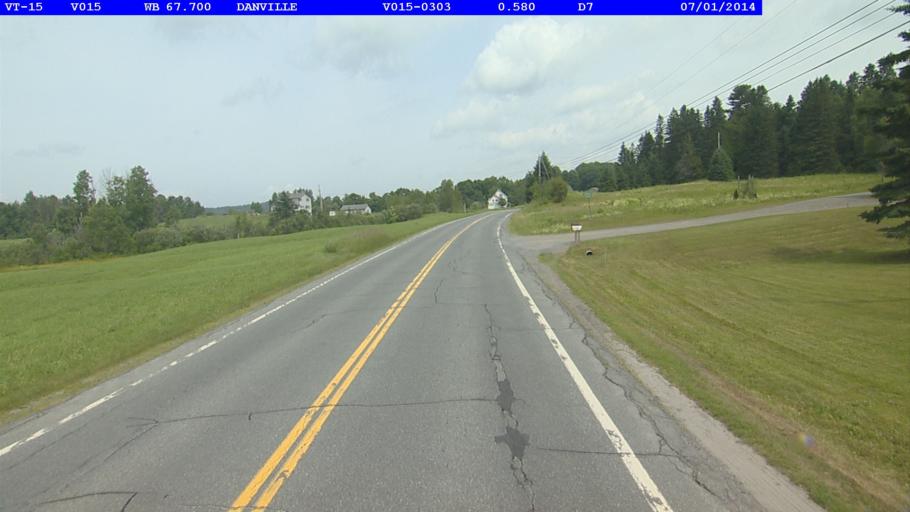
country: US
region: Vermont
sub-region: Caledonia County
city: Hardwick
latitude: 44.4145
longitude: -72.2169
